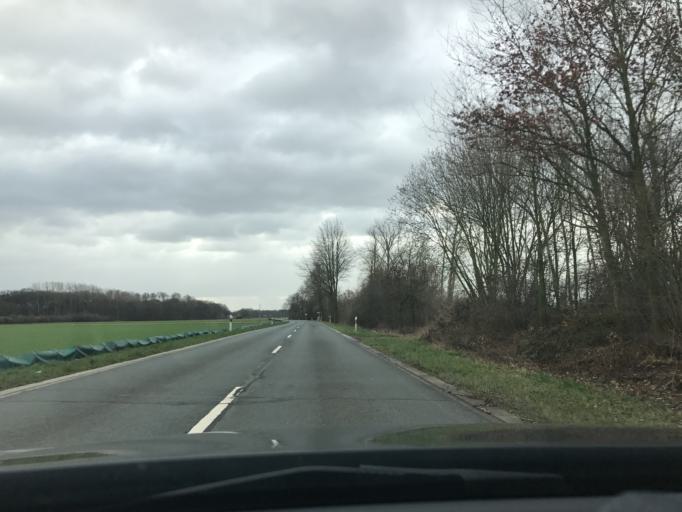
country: DE
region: North Rhine-Westphalia
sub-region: Regierungsbezirk Dusseldorf
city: Wachtendonk
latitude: 51.4383
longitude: 6.3414
